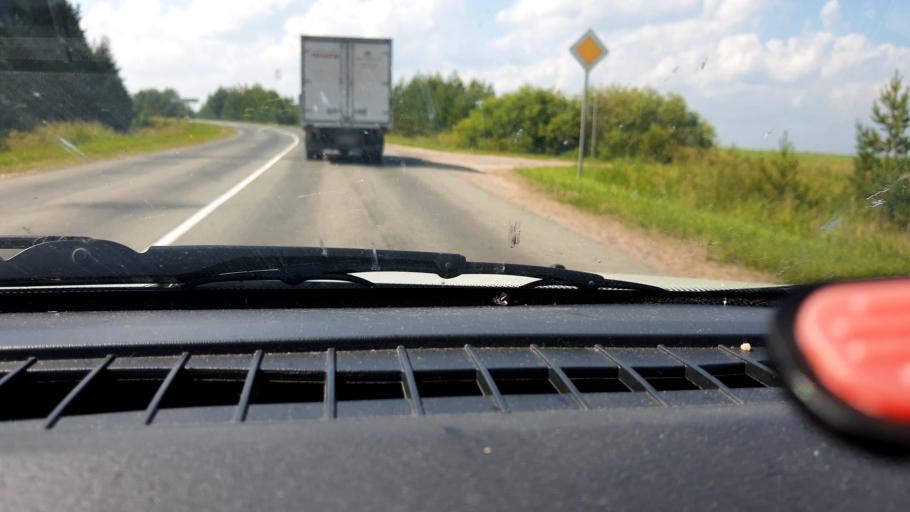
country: RU
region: Nizjnij Novgorod
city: Tonkino
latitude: 57.3743
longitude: 46.3676
